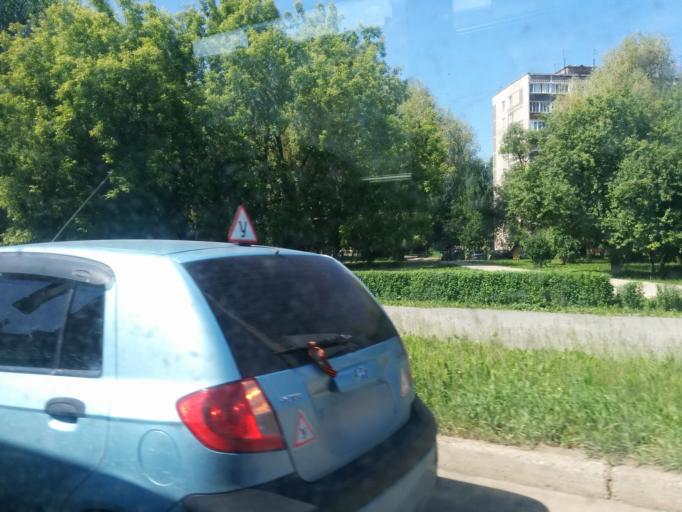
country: RU
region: Perm
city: Perm
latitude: 57.9999
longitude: 56.2963
